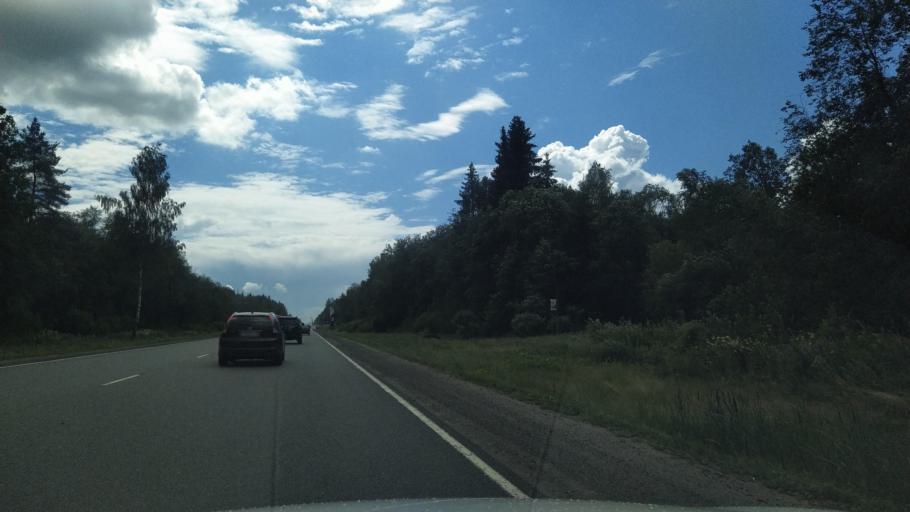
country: RU
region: Leningrad
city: Rozhdestveno
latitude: 59.3920
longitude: 29.9712
